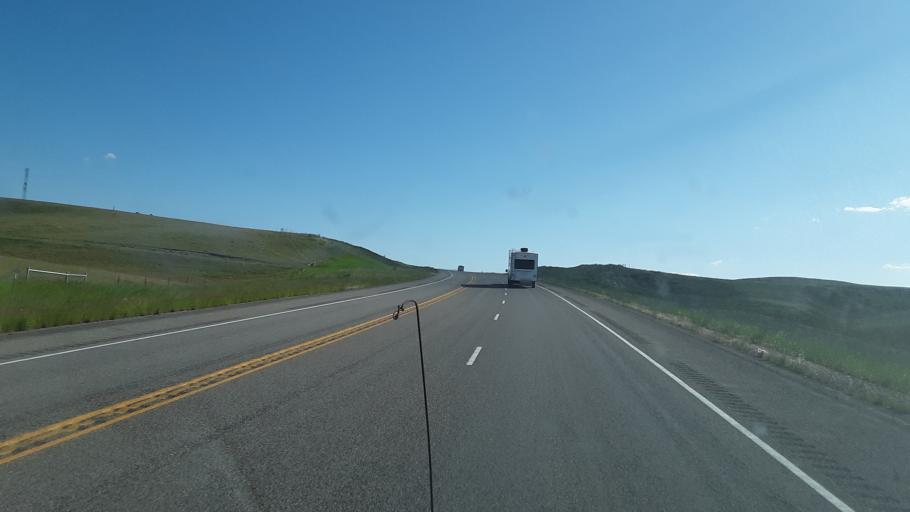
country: US
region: Montana
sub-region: Wheatland County
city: Harlowton
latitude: 46.4411
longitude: -109.8023
